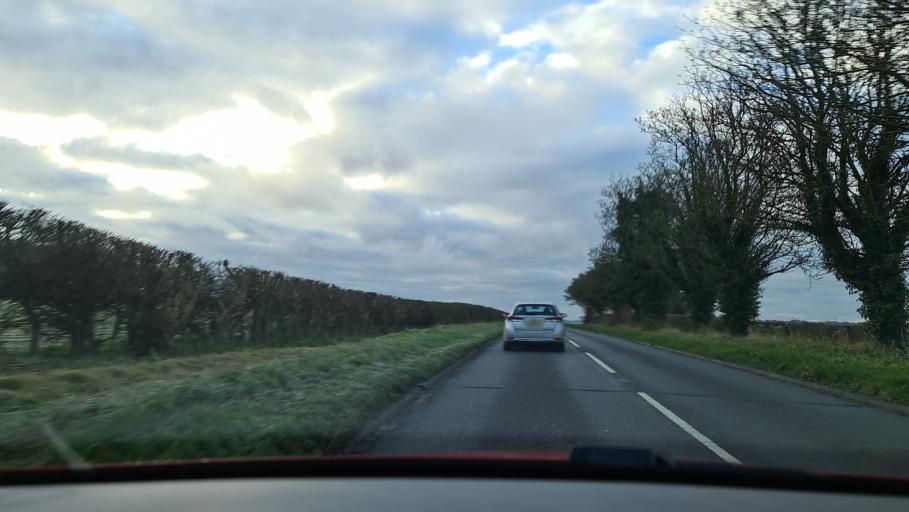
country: GB
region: England
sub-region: Buckinghamshire
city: Princes Risborough
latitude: 51.7078
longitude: -0.8335
